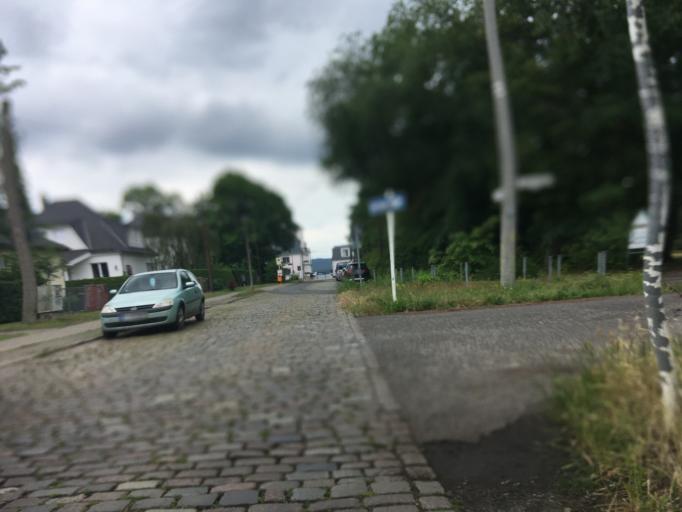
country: DE
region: Berlin
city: Friedrichshagen
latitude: 52.4488
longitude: 13.6404
